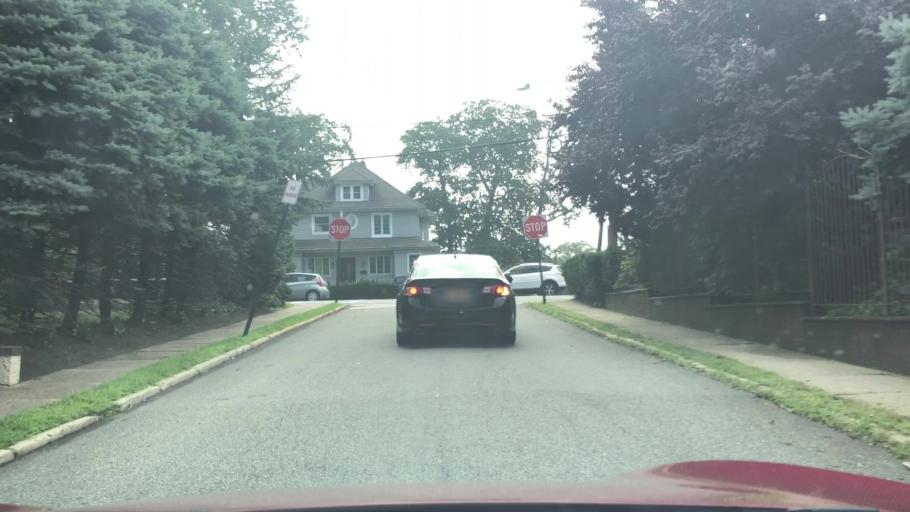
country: US
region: New Jersey
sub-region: Bergen County
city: Edgewater
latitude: 40.8348
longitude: -73.9841
